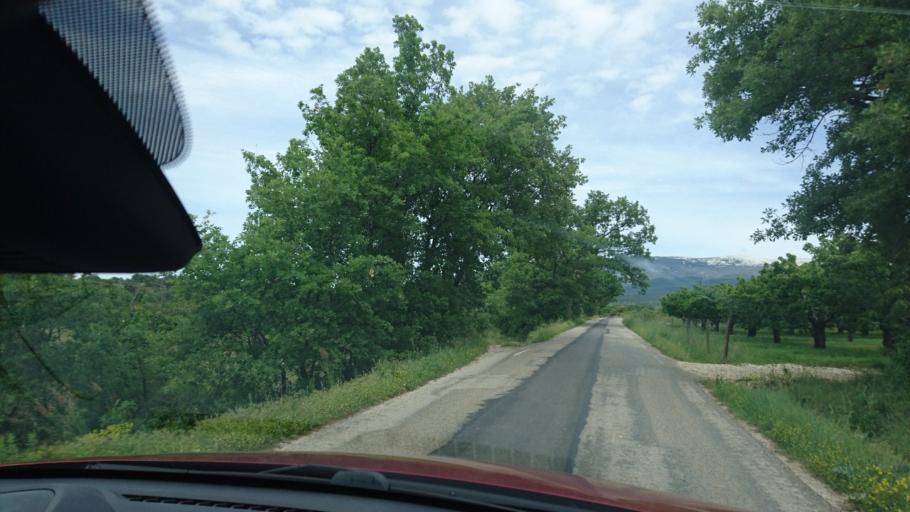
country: FR
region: Provence-Alpes-Cote d'Azur
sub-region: Departement du Vaucluse
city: Villes-sur-Auzon
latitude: 44.0777
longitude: 5.2348
